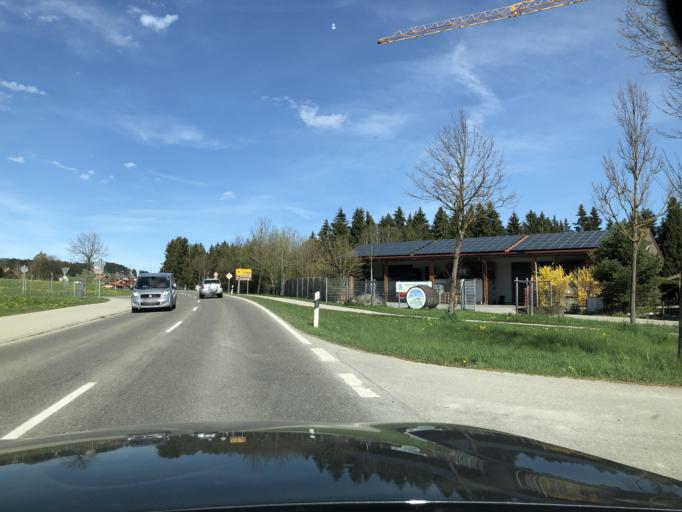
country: DE
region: Bavaria
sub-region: Swabia
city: Hopferau
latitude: 47.6134
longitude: 10.6233
